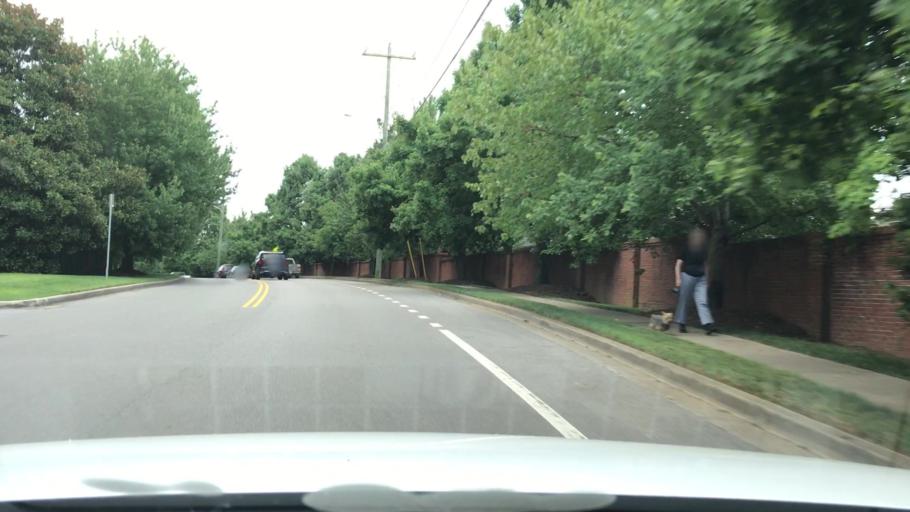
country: US
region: Tennessee
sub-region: Davidson County
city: Belle Meade
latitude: 36.1288
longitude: -86.8187
